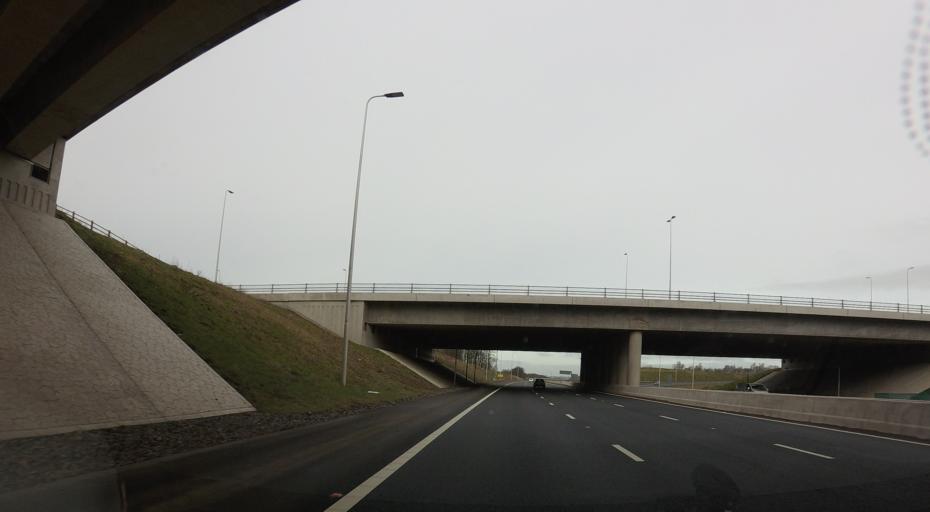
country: GB
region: Scotland
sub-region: North Lanarkshire
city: Bellshill
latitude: 55.8378
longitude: -4.0241
